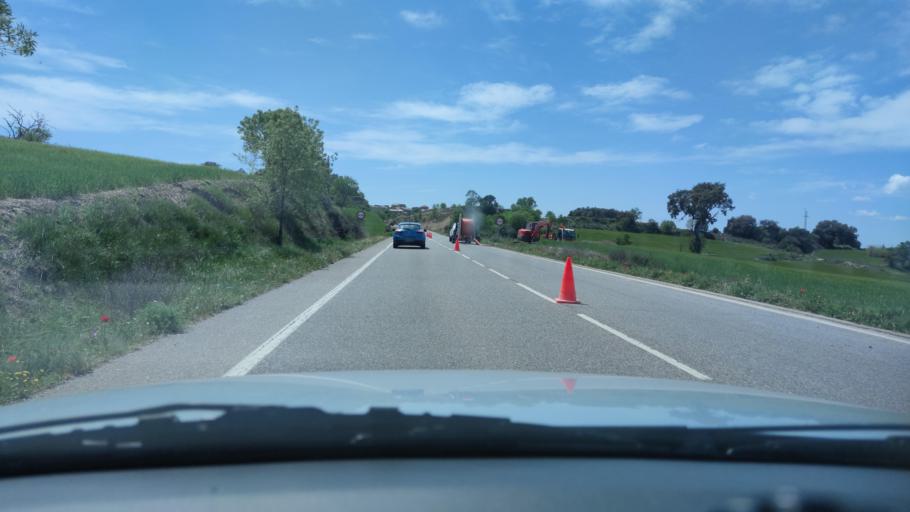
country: ES
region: Catalonia
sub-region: Provincia de Lleida
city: Mont-roig del Camp
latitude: 41.7702
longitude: 1.2568
